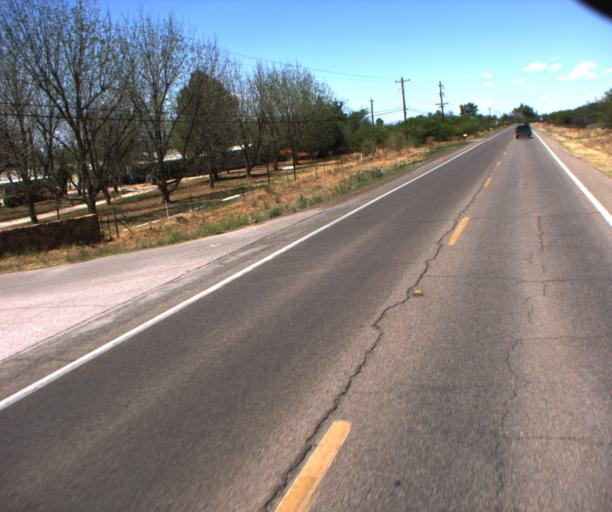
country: US
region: Arizona
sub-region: Cochise County
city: Saint David
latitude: 31.8770
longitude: -110.2109
